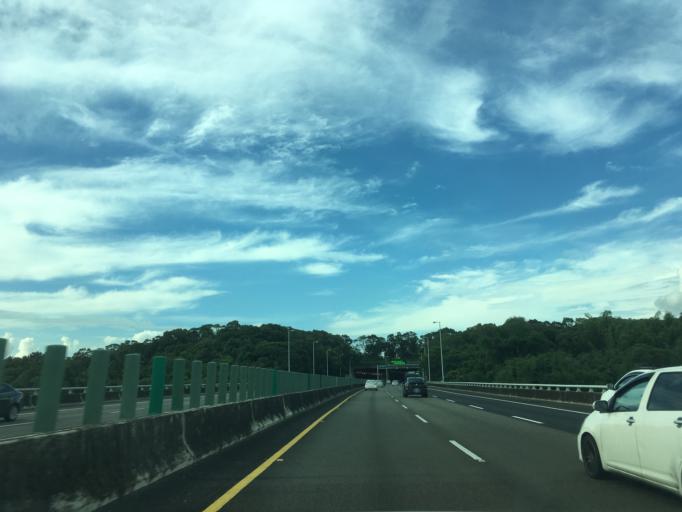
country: TW
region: Taiwan
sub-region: Chiayi
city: Jiayi Shi
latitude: 23.5736
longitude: 120.5065
